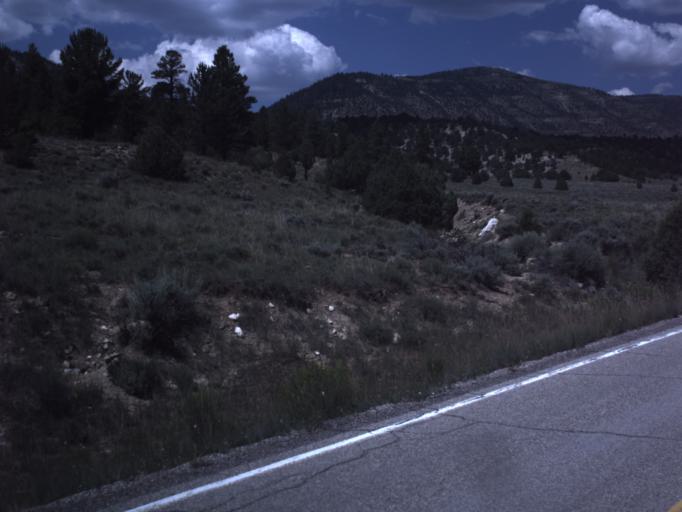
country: US
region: Utah
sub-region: Emery County
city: Orangeville
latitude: 39.3165
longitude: -111.2830
